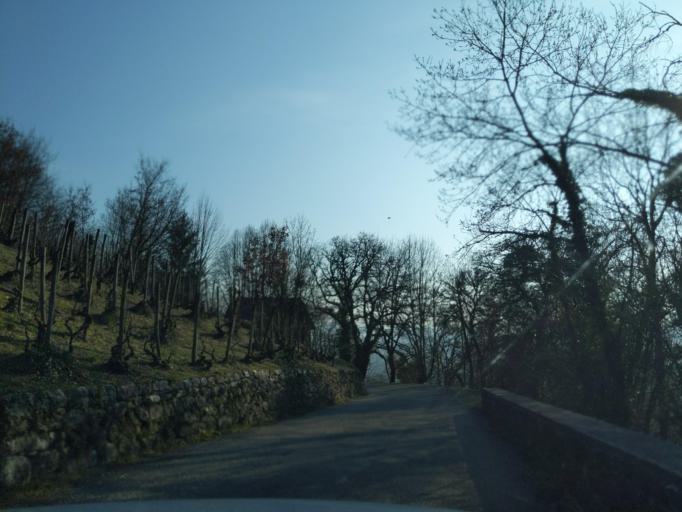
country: FR
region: Rhone-Alpes
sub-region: Departement de la Haute-Savoie
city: Moye
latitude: 45.8899
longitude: 5.8485
